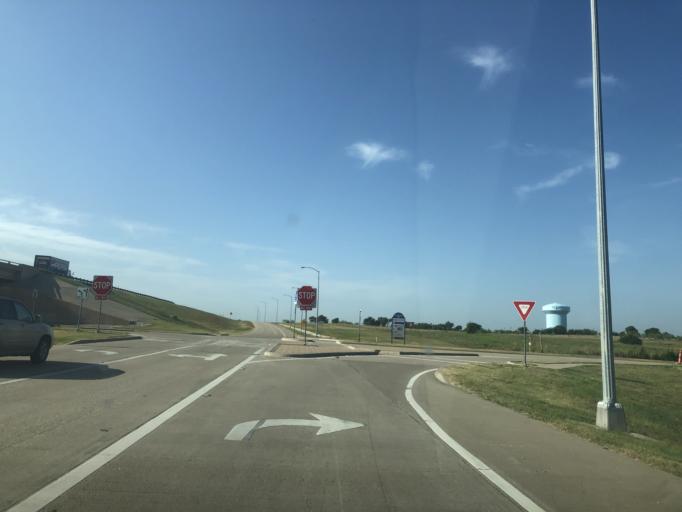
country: US
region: Texas
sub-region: Tarrant County
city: Crowley
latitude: 32.6070
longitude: -97.4133
